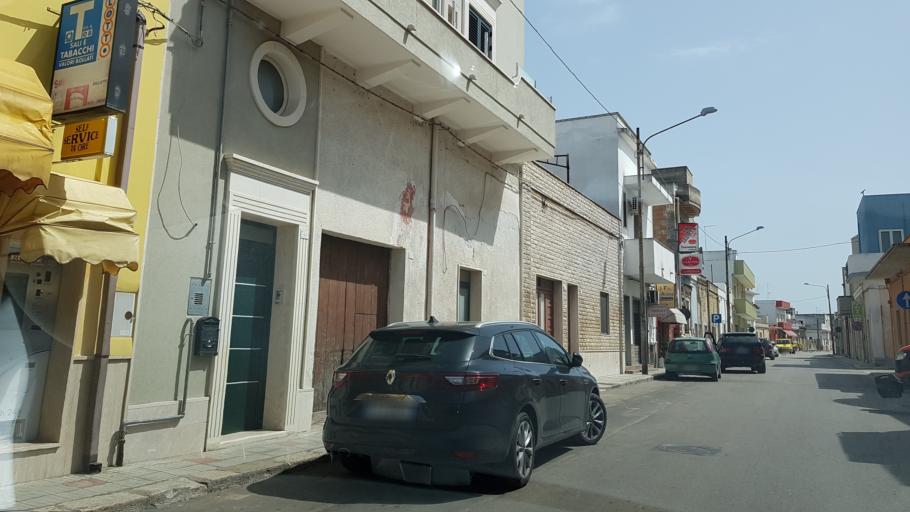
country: IT
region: Apulia
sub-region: Provincia di Brindisi
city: San Pancrazio Salentino
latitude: 40.4156
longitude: 17.8394
